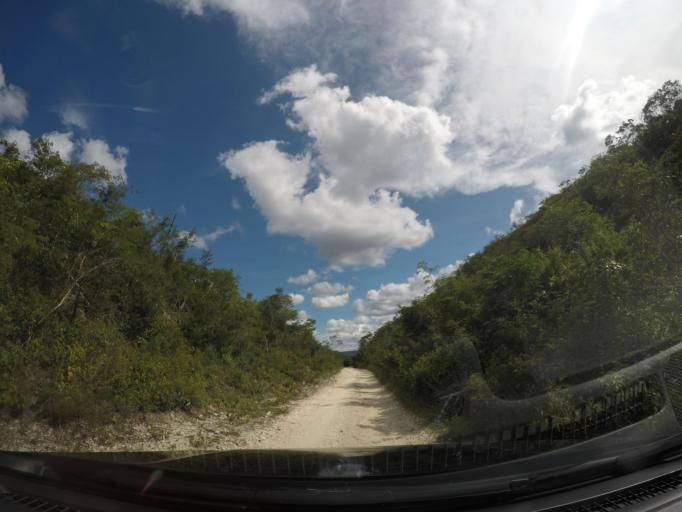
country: BR
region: Bahia
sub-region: Barra Da Estiva
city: Barra da Estiva
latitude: -13.1334
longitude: -41.5945
